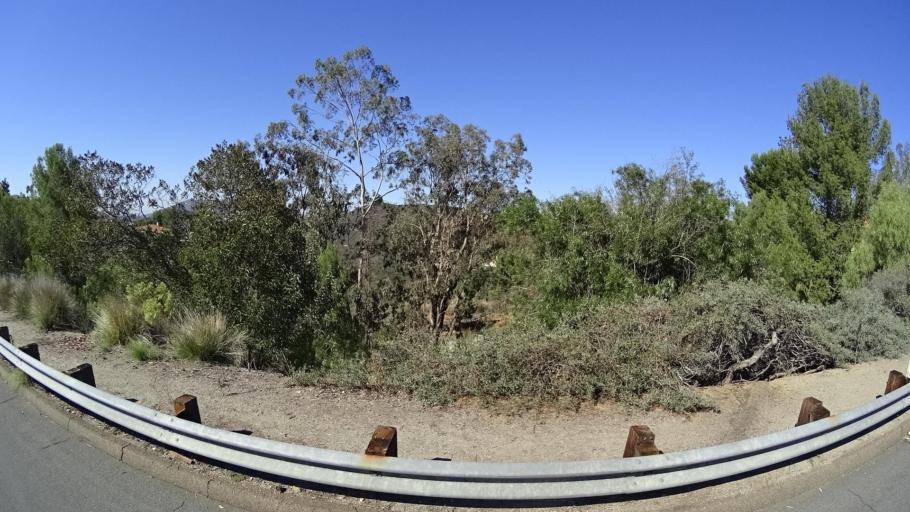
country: US
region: California
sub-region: San Diego County
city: Jamul
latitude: 32.7371
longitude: -116.8542
